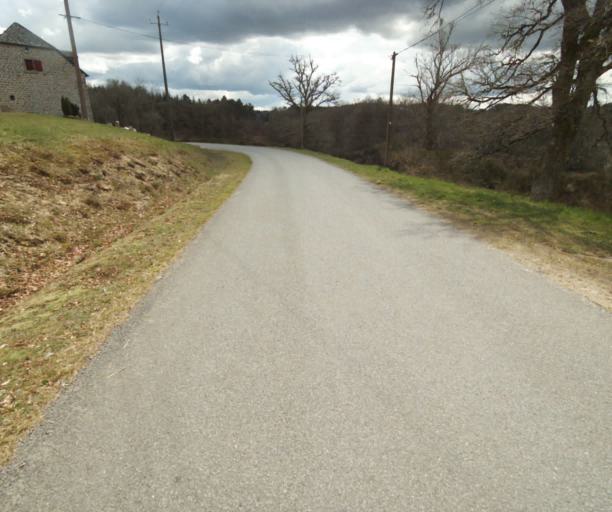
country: FR
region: Limousin
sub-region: Departement de la Correze
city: Correze
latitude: 45.3123
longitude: 1.9317
